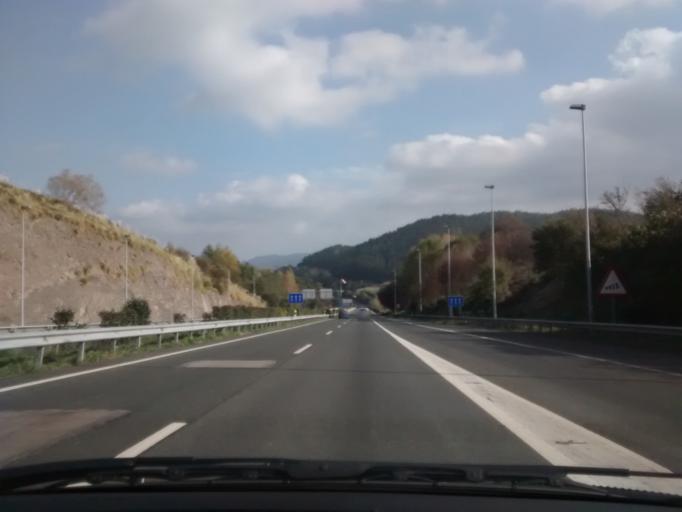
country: ES
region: Cantabria
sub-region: Provincia de Cantabria
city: Lierganes
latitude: 43.3885
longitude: -3.7377
